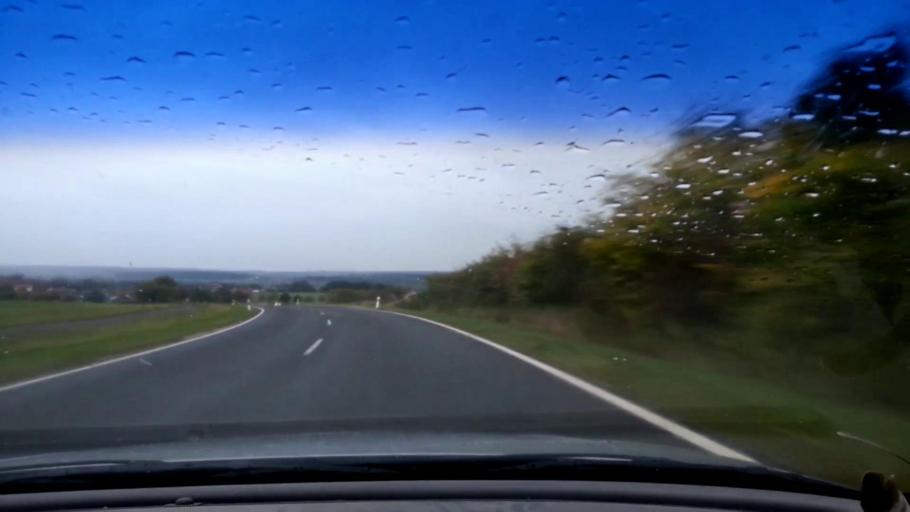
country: DE
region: Bavaria
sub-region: Upper Franconia
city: Priesendorf
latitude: 49.8687
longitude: 10.7157
